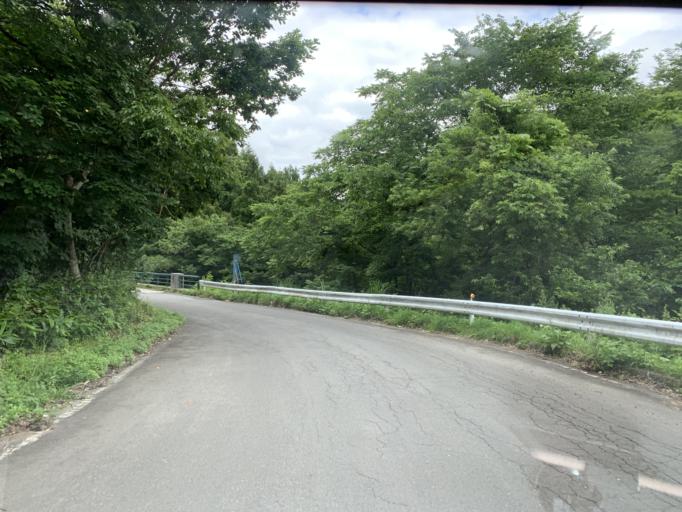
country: JP
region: Iwate
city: Ichinoseki
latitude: 38.9629
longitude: 140.9008
